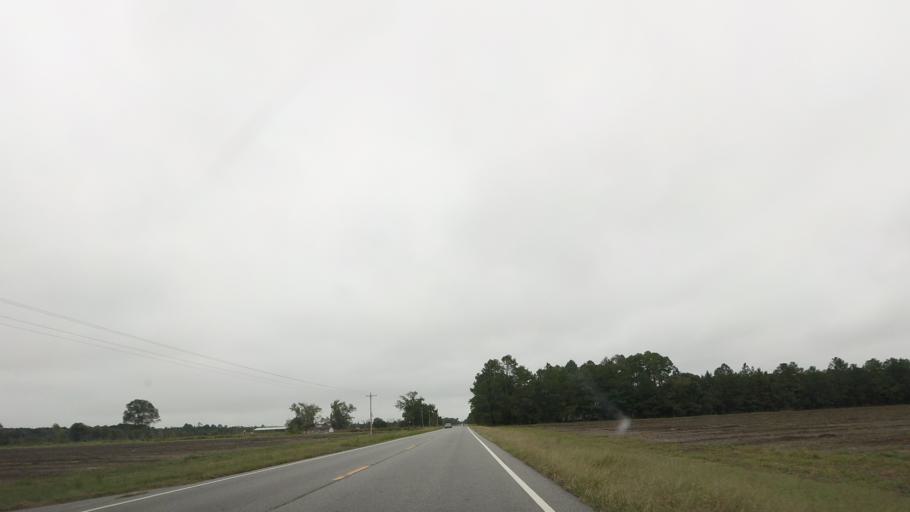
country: US
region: Georgia
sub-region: Berrien County
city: Nashville
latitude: 31.3105
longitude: -83.2322
